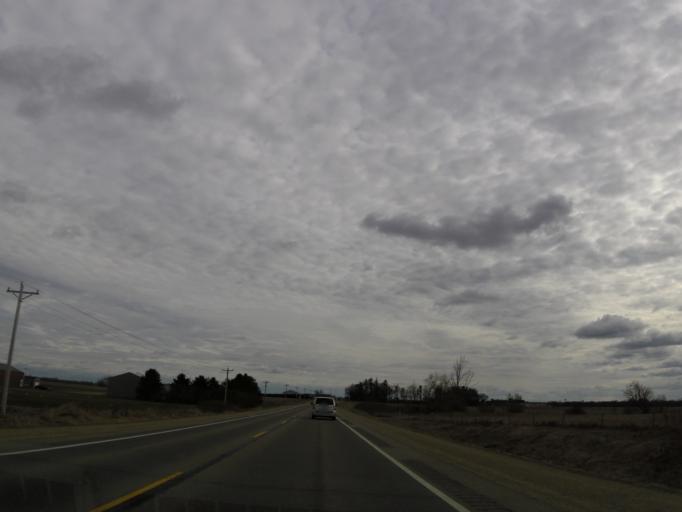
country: US
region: Iowa
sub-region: Chickasaw County
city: New Hampton
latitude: 43.1005
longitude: -92.2979
